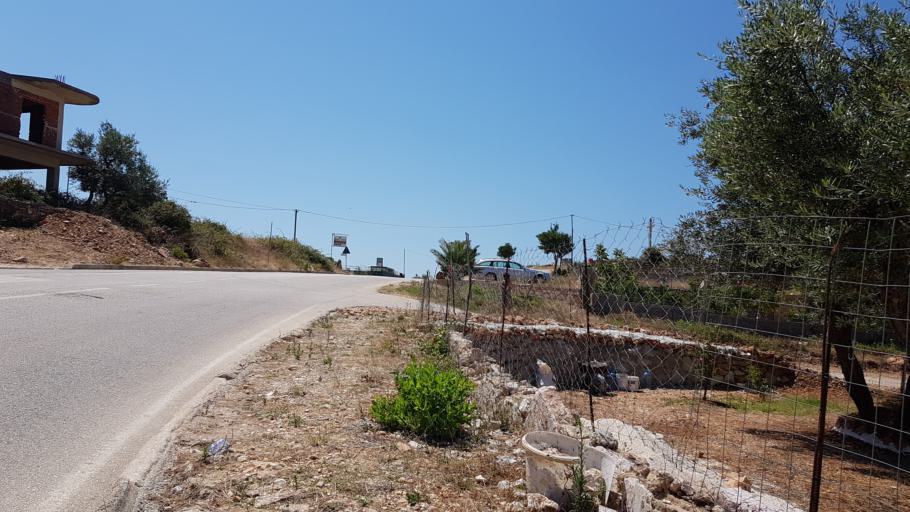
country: AL
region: Vlore
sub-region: Rrethi i Sarandes
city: Xarre
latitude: 39.7635
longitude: 20.0017
